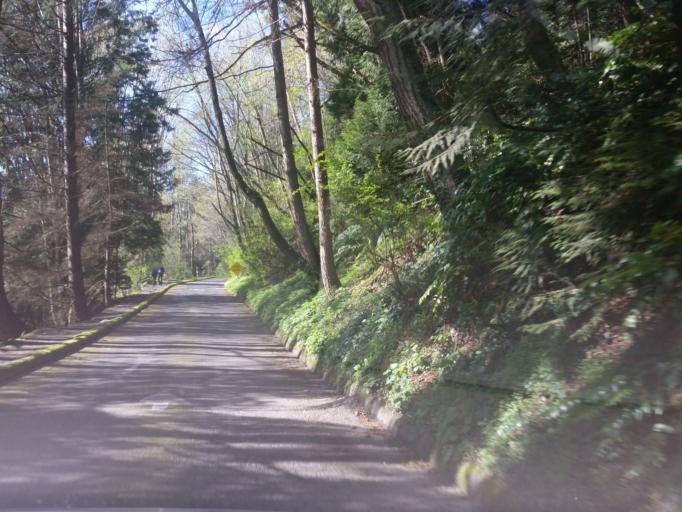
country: US
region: Washington
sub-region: King County
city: Shoreline
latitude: 47.7114
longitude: -122.3724
